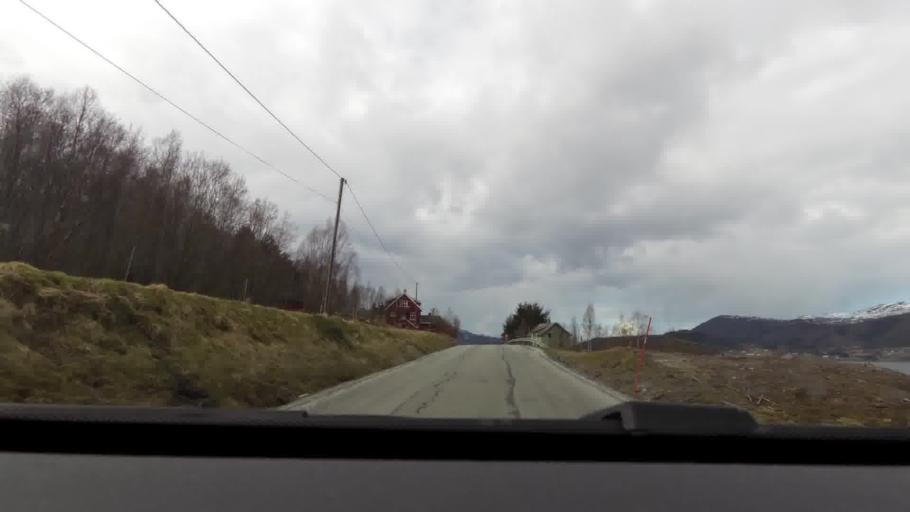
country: NO
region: More og Romsdal
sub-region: Kristiansund
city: Kristiansund
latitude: 63.1133
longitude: 7.7544
